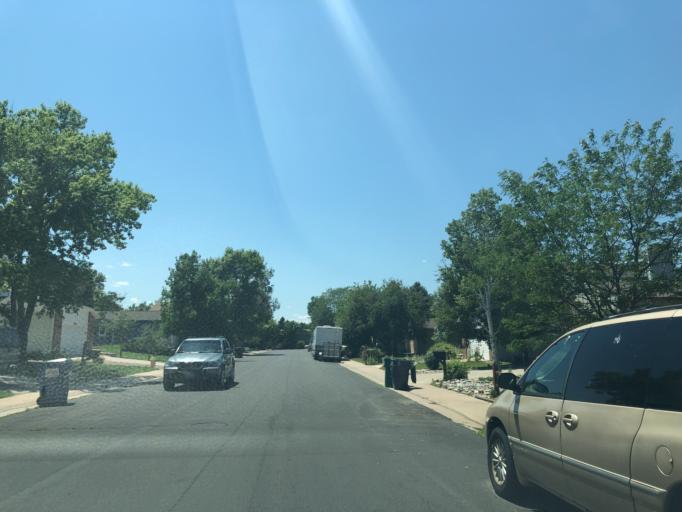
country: US
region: Colorado
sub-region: Arapahoe County
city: Dove Valley
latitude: 39.6236
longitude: -104.7755
